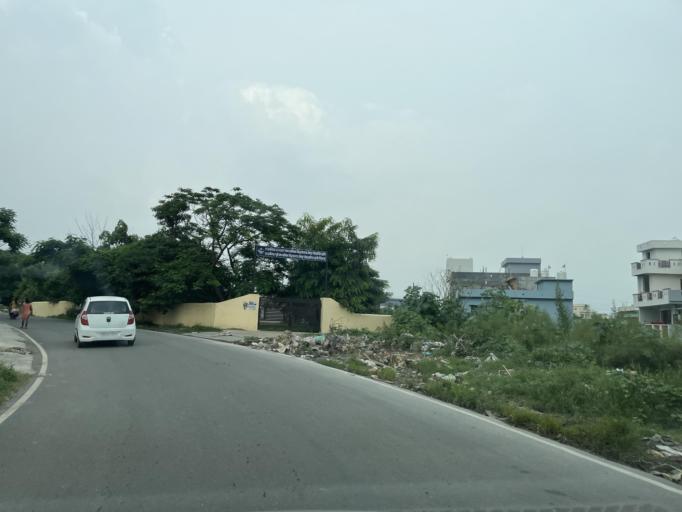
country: IN
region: Uttarakhand
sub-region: Naini Tal
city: Haldwani
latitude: 29.1888
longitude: 79.4789
